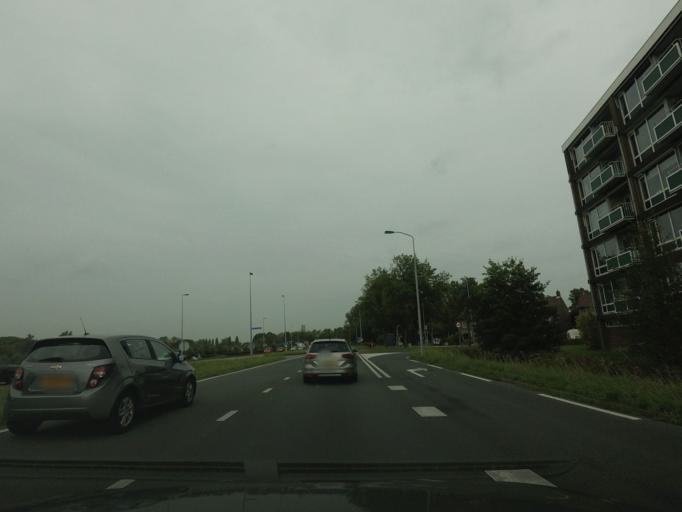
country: NL
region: North Holland
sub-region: Gemeente Zaanstad
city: Zaanstad
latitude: 52.4782
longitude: 4.8060
